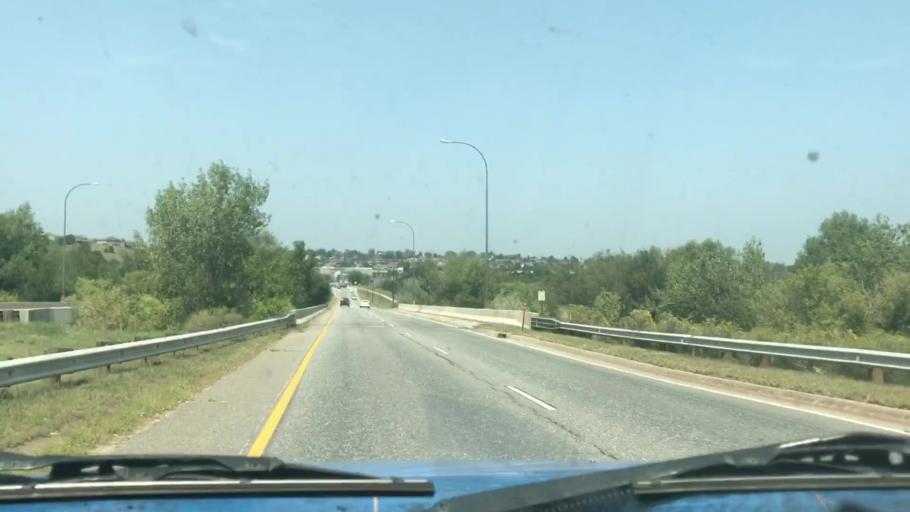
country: US
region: Colorado
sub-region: Jefferson County
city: Lakewood
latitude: 39.6615
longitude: -105.1125
